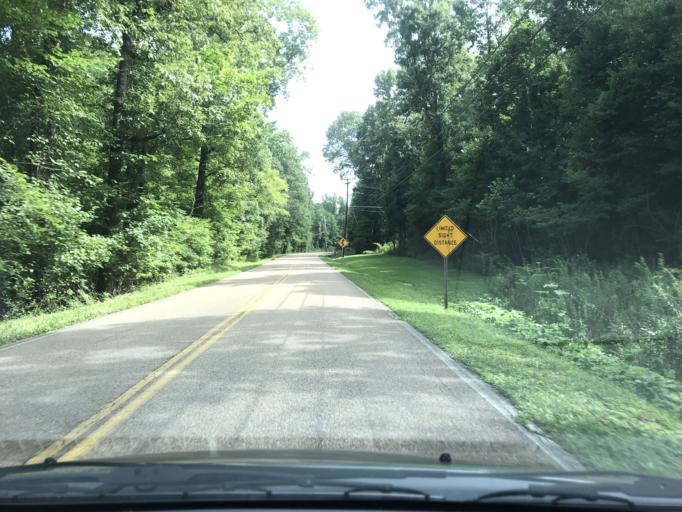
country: US
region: Tennessee
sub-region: Hamilton County
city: Lakesite
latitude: 35.1818
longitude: -85.1122
